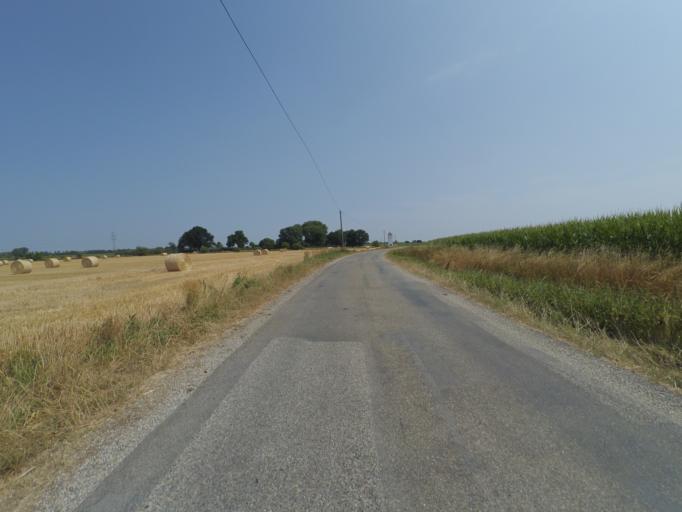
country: DE
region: North Rhine-Westphalia
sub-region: Regierungsbezirk Dusseldorf
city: Mehrhoog
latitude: 51.7359
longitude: 6.4626
